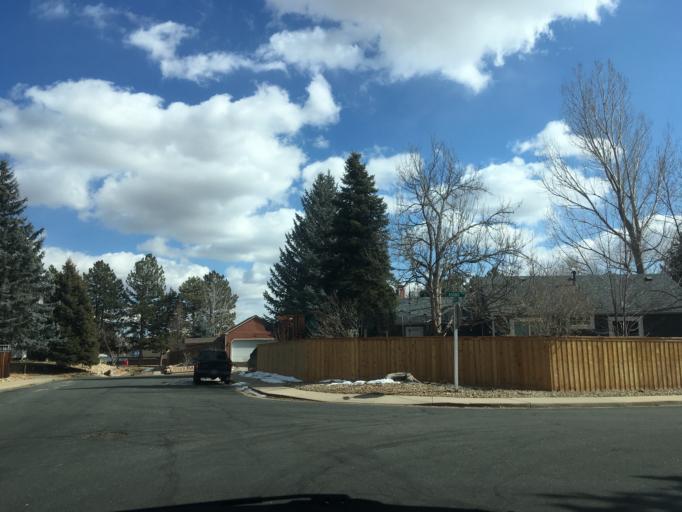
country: US
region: Colorado
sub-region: Boulder County
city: Louisville
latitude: 39.9754
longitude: -105.1412
